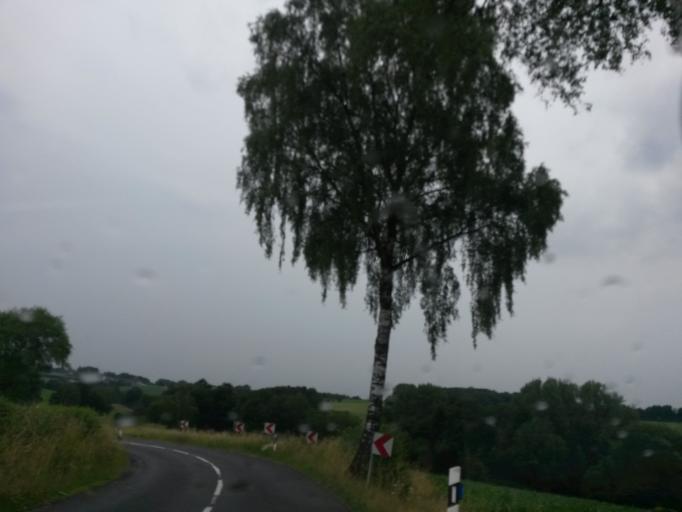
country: DE
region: North Rhine-Westphalia
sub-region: Regierungsbezirk Koln
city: Much
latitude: 50.9324
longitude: 7.3781
